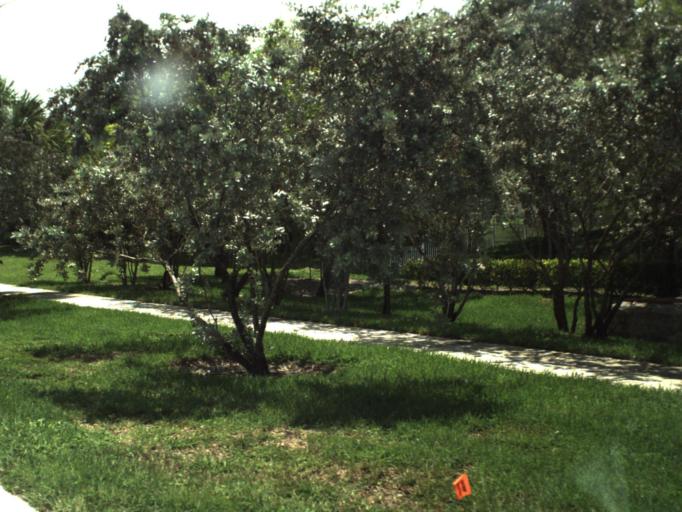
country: US
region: Florida
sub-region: Broward County
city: Coral Springs
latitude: 26.2853
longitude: -80.2504
